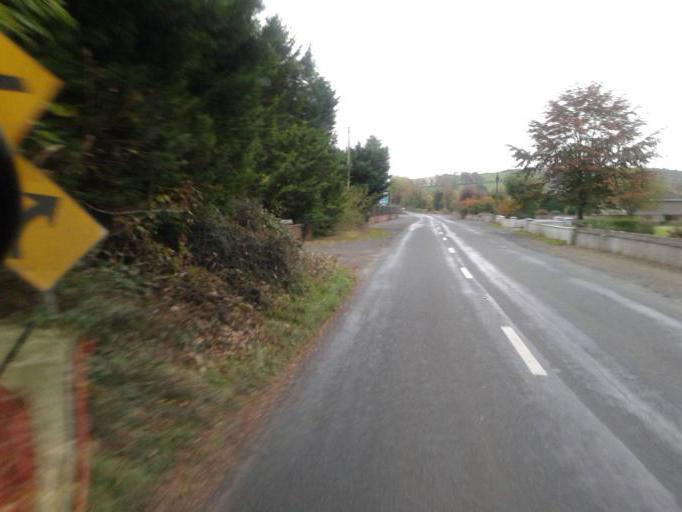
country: IE
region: Munster
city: Ballina
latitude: 52.7755
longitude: -8.4310
